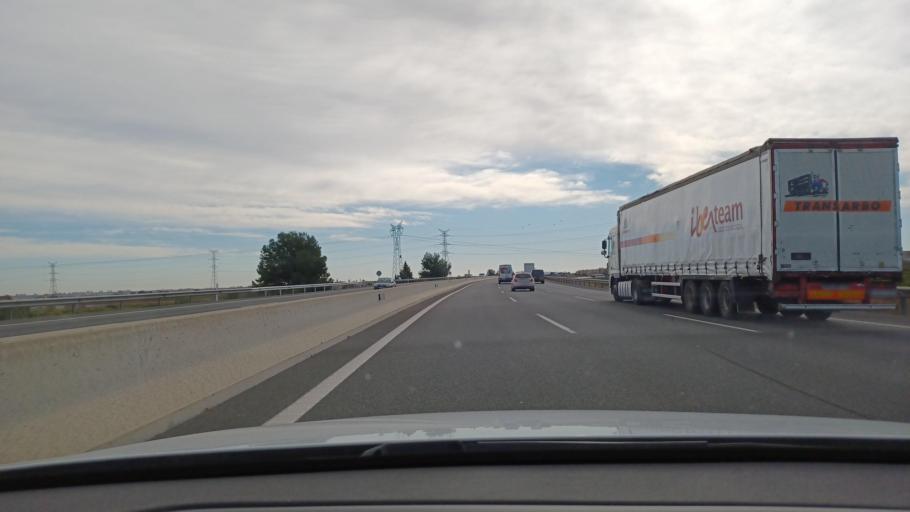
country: ES
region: Valencia
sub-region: Provincia de Valencia
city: Picassent
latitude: 39.3831
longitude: -0.4713
